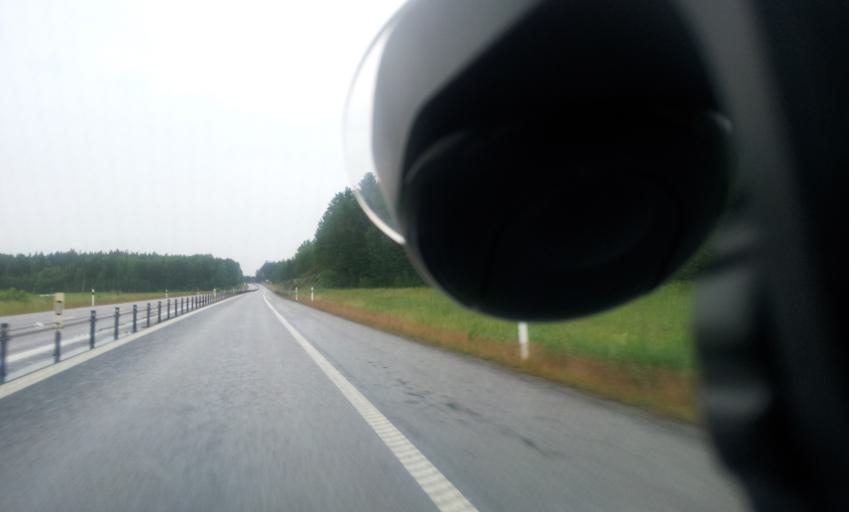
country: SE
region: OEstergoetland
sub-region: Valdemarsviks Kommun
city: Gusum
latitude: 58.2452
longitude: 16.5385
